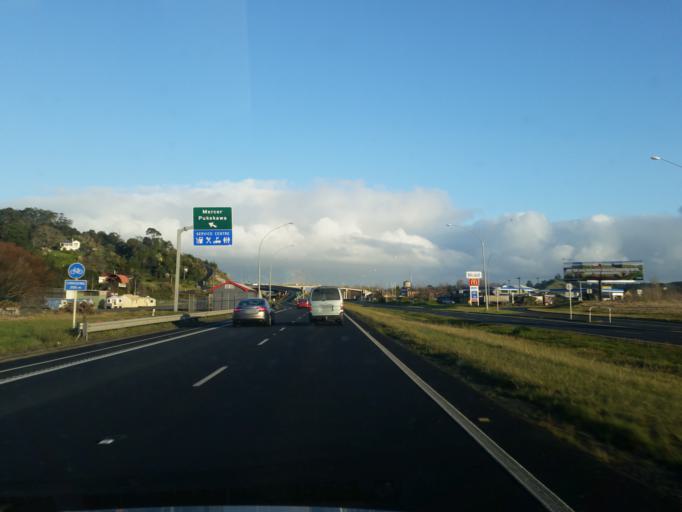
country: NZ
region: Auckland
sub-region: Auckland
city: Pukekohe East
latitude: -37.2754
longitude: 175.0469
